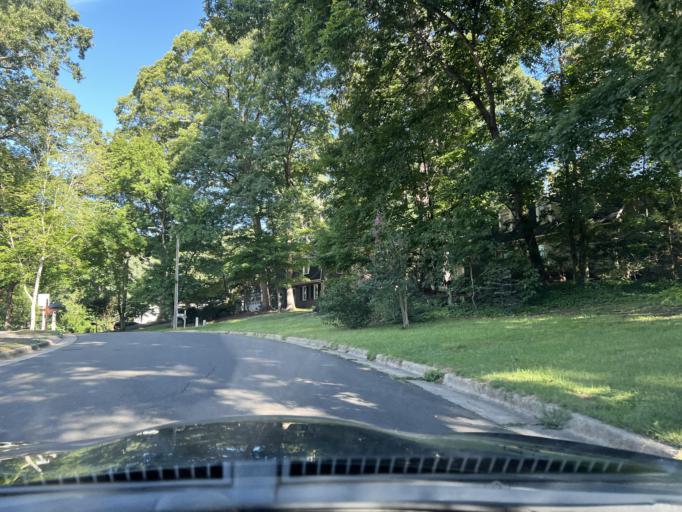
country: US
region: North Carolina
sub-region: Wake County
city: West Raleigh
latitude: 35.8428
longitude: -78.6208
